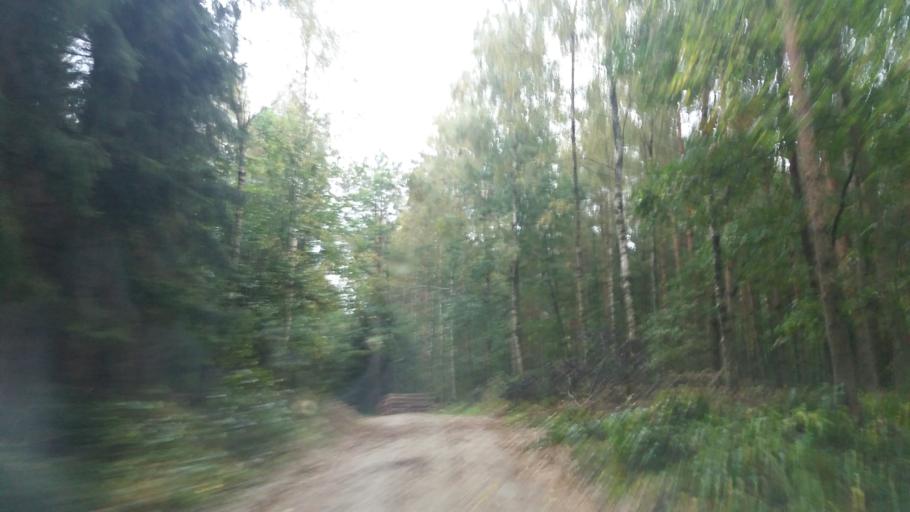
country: PL
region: West Pomeranian Voivodeship
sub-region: Powiat choszczenski
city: Pelczyce
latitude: 53.0762
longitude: 15.2663
